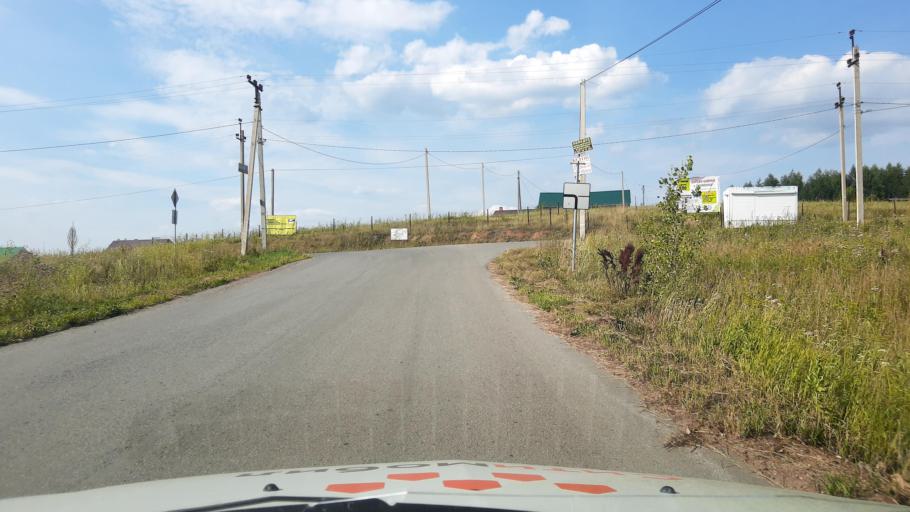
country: RU
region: Bashkortostan
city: Kabakovo
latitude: 54.6664
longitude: 56.2139
